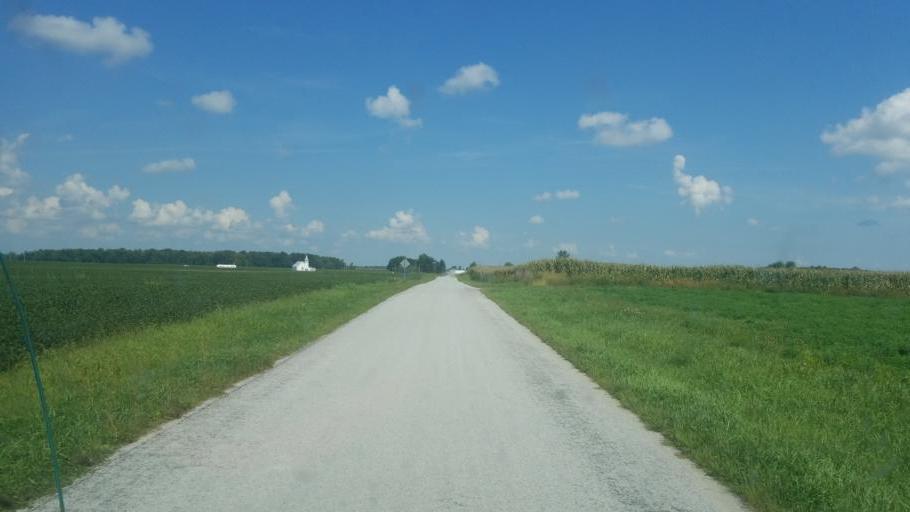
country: US
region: Ohio
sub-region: Hardin County
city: Kenton
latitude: 40.6810
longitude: -83.4957
